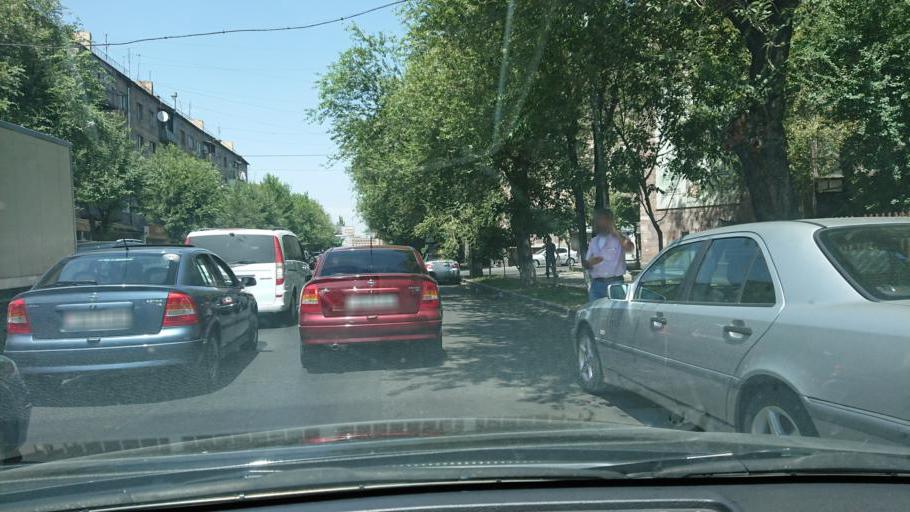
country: AM
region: Yerevan
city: Yerevan
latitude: 40.2036
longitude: 44.4983
